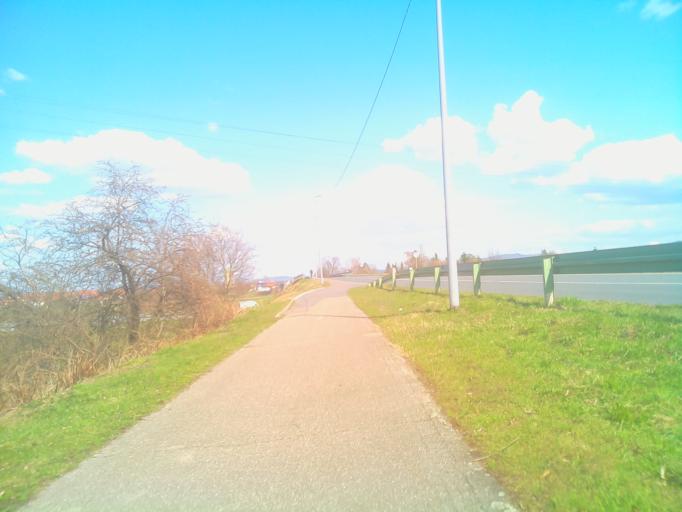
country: DE
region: Baden-Wuerttemberg
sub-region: Karlsruhe Region
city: Ilvesheim
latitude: 49.4570
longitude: 8.5461
